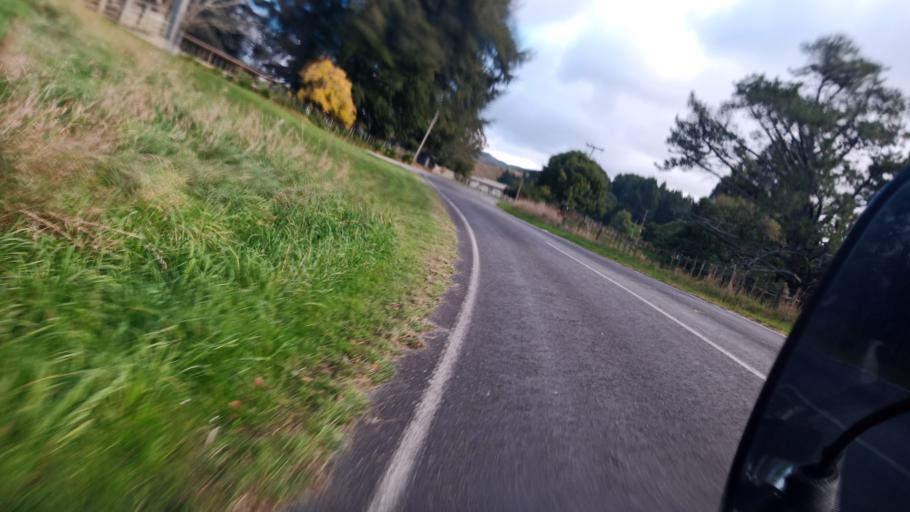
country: NZ
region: Gisborne
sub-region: Gisborne District
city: Gisborne
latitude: -38.5375
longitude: 177.5602
